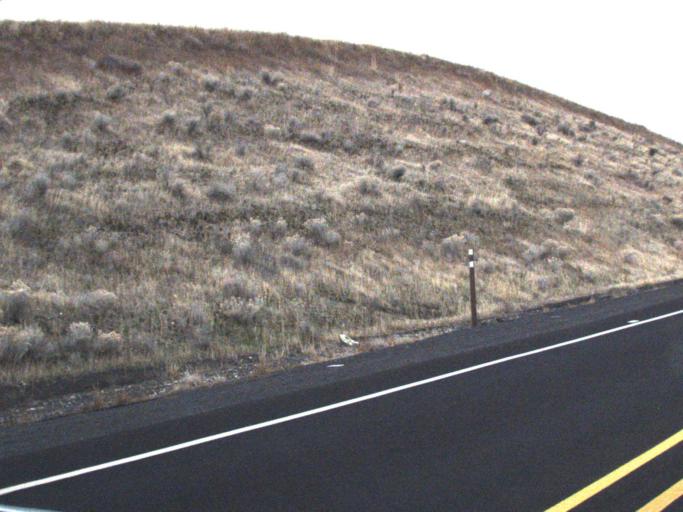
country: US
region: Washington
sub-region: Adams County
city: Ritzville
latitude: 46.7936
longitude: -118.3910
